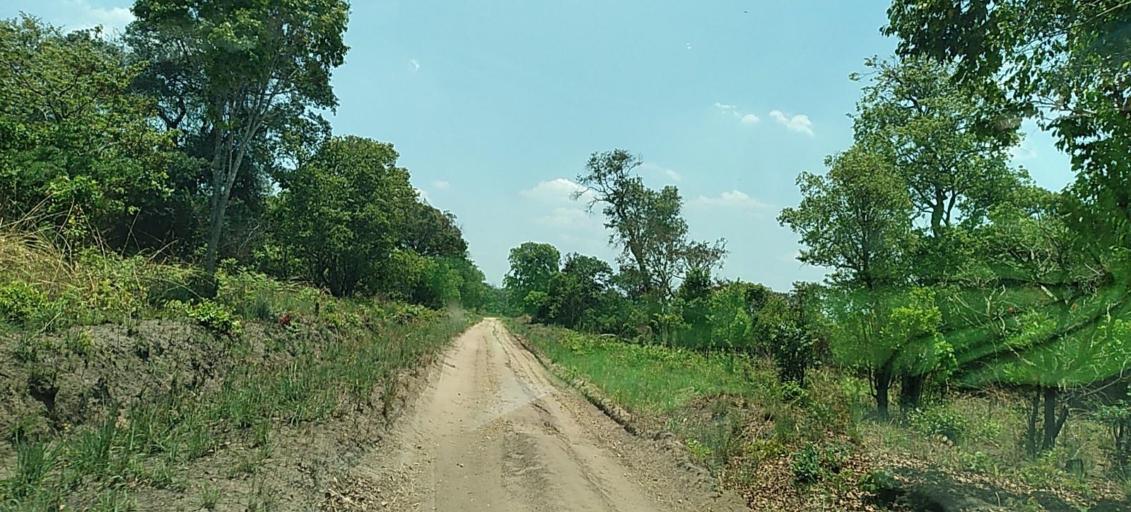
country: CD
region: Katanga
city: Kolwezi
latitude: -11.3669
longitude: 25.2094
